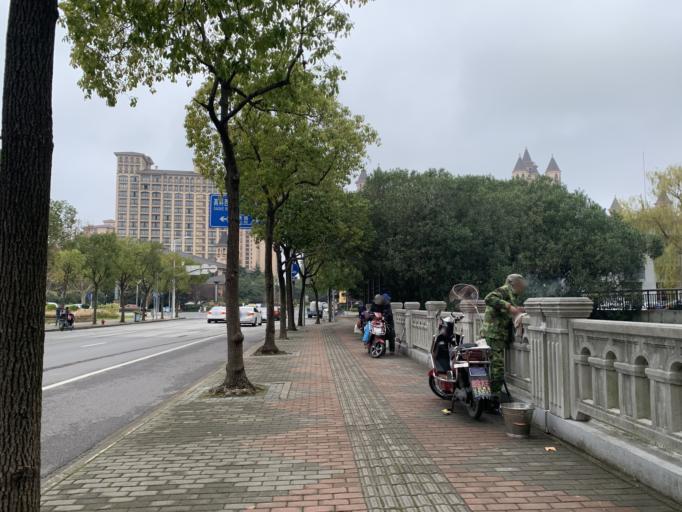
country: CN
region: Shanghai Shi
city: Huamu
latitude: 31.1949
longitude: 121.5358
